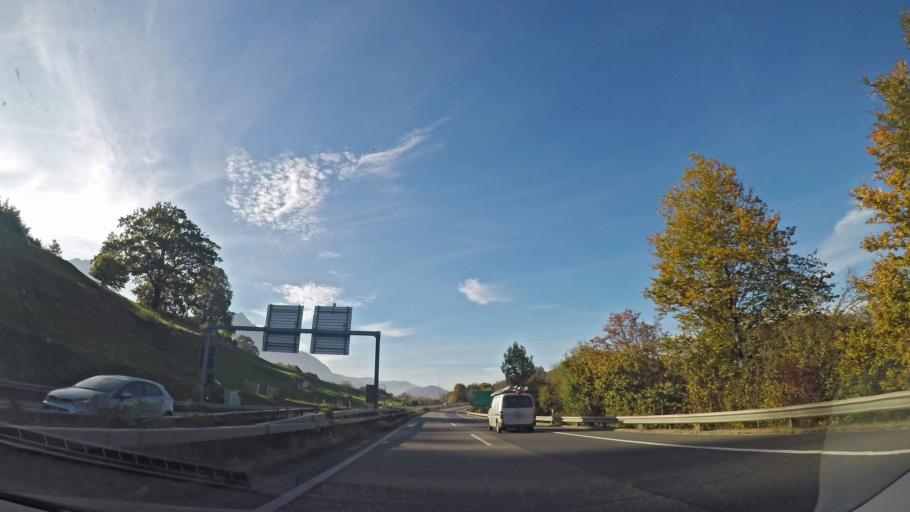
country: CH
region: Bern
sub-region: Frutigen-Niedersimmental District
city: Wimmis
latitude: 46.6894
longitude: 7.6610
